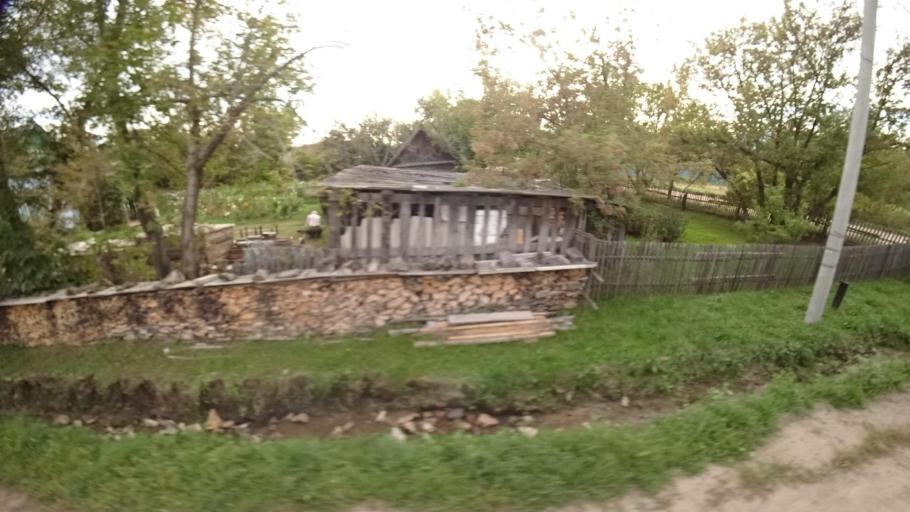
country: RU
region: Primorskiy
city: Yakovlevka
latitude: 44.4207
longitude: 133.4621
